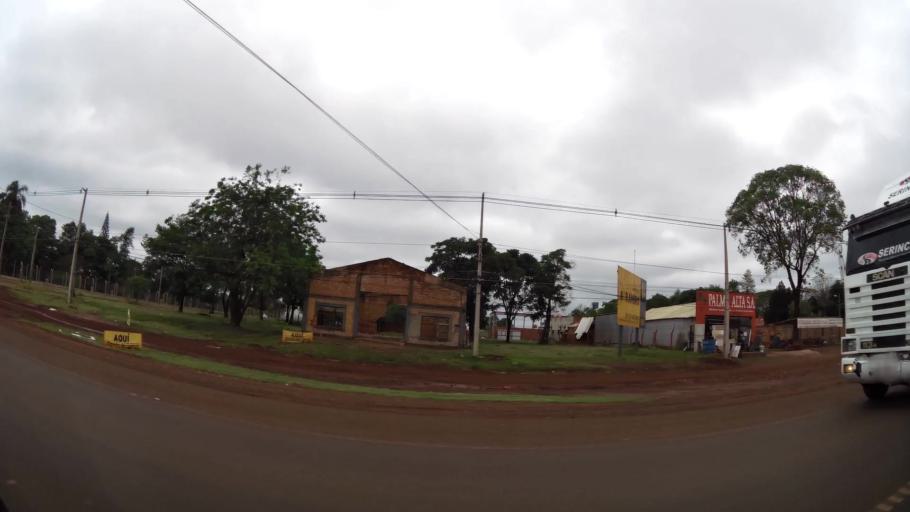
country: PY
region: Alto Parana
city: Ciudad del Este
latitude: -25.4927
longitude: -54.7300
